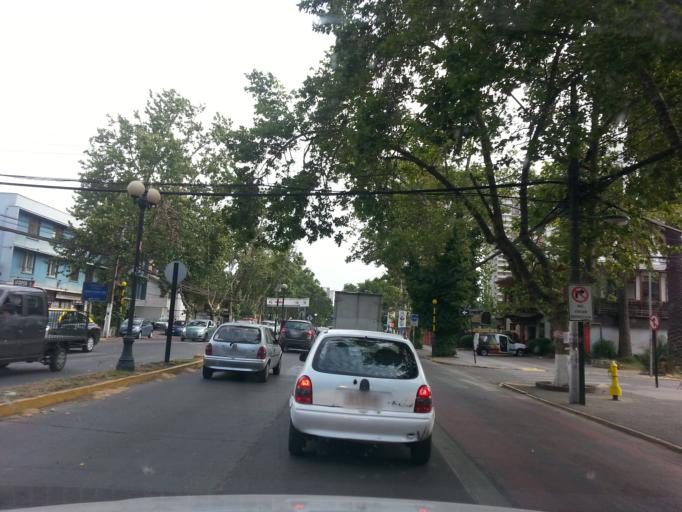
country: CL
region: Santiago Metropolitan
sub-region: Provincia de Santiago
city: Villa Presidente Frei, Nunoa, Santiago, Chile
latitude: -33.4780
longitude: -70.5991
